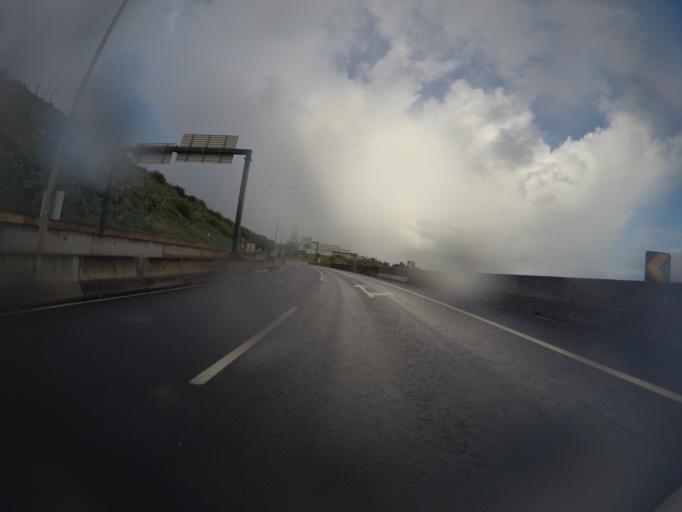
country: PT
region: Madeira
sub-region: Santa Cruz
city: Santa Cruz
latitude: 32.6883
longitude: -16.7837
